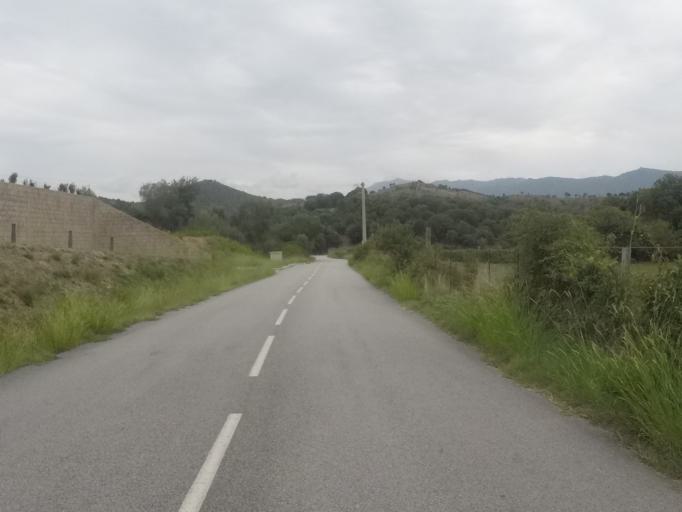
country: FR
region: Corsica
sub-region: Departement de la Corse-du-Sud
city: Pietrosella
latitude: 41.7494
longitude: 8.8194
